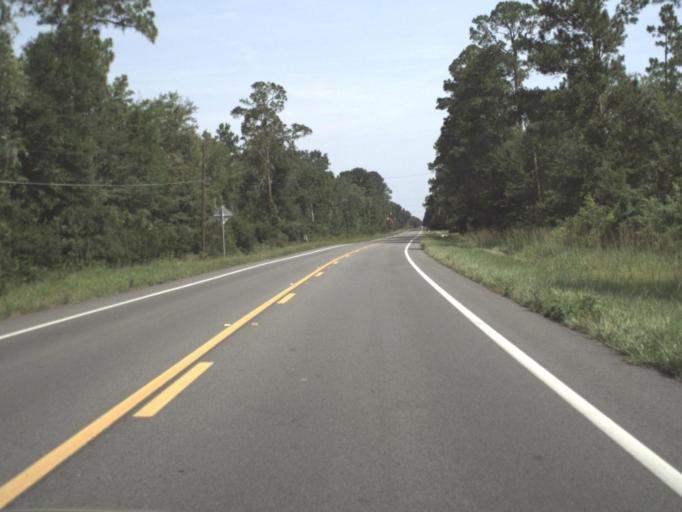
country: US
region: Florida
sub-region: Hamilton County
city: Jasper
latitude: 30.5317
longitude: -82.9697
